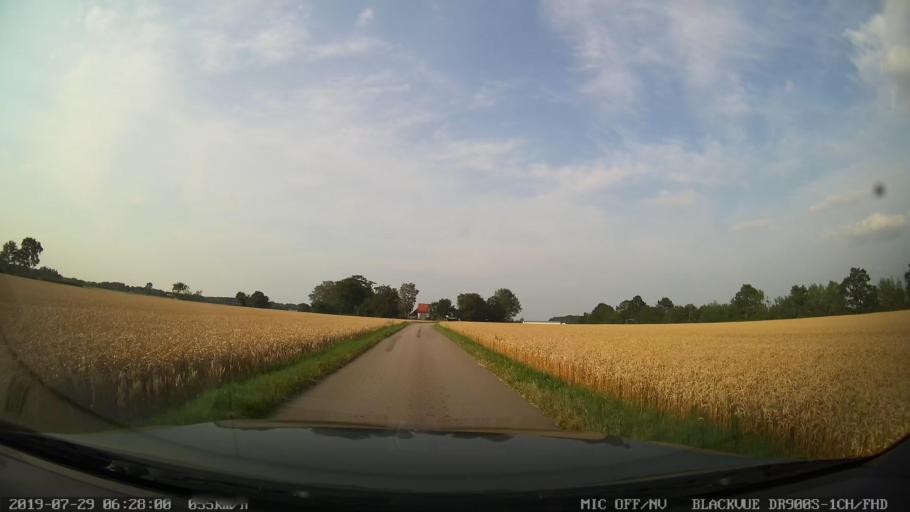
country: SE
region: Skane
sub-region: Helsingborg
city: Odakra
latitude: 56.1112
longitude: 12.7151
